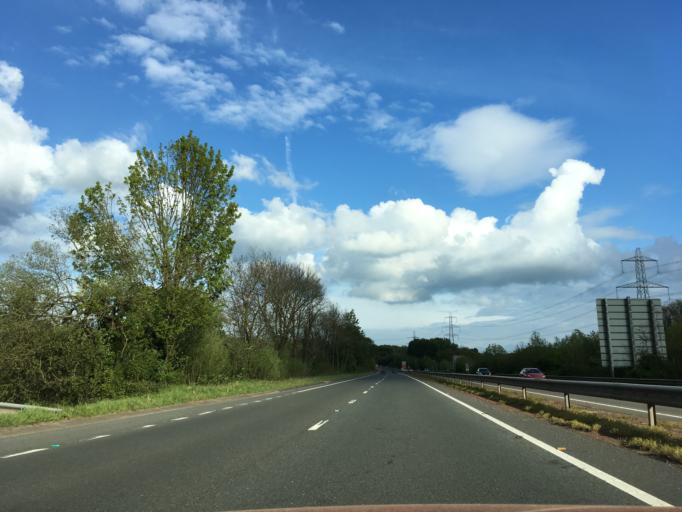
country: GB
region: Wales
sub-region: Monmouthshire
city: Abergavenny
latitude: 51.8130
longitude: -3.0205
